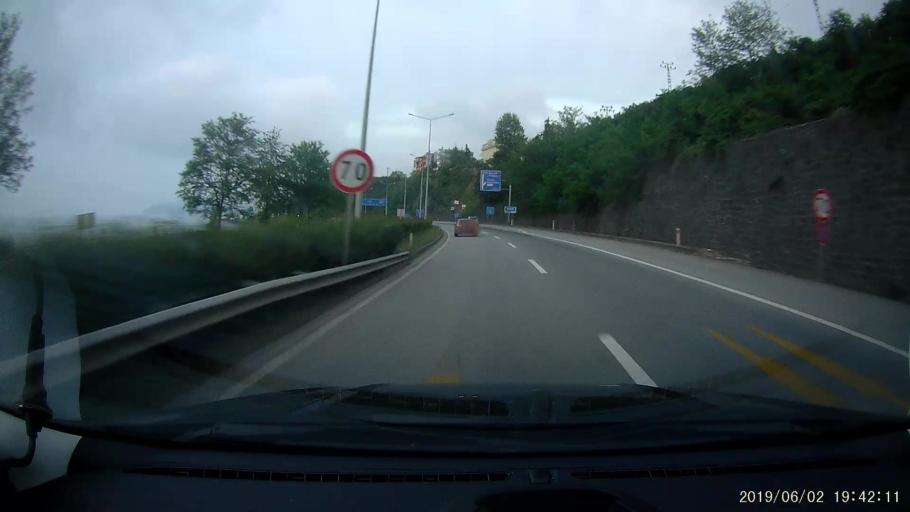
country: TR
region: Giresun
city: Kesap
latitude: 40.9157
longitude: 38.4979
